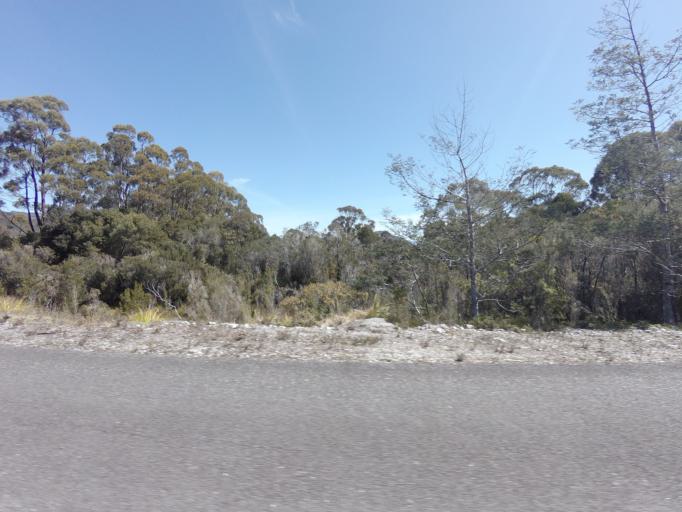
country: AU
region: Tasmania
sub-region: Huon Valley
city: Geeveston
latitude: -42.8423
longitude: 146.1638
